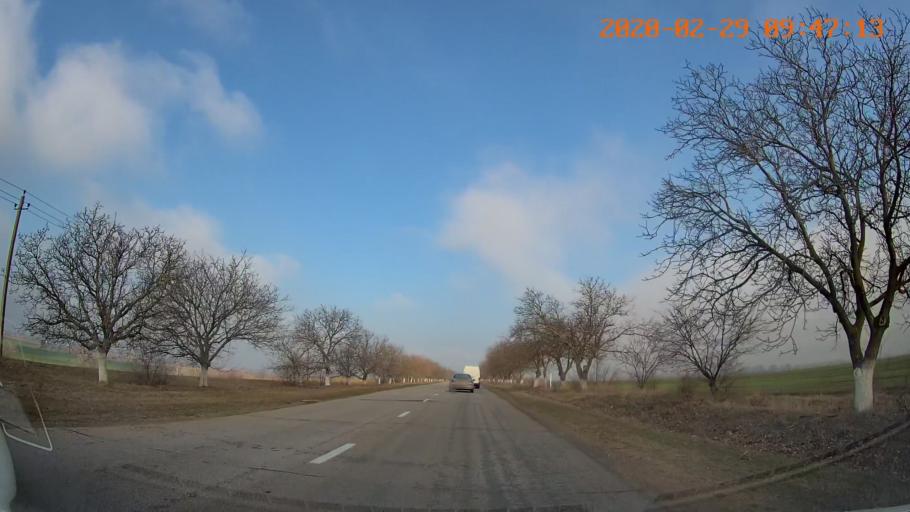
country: MD
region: Telenesti
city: Crasnoe
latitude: 46.6753
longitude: 29.7922
